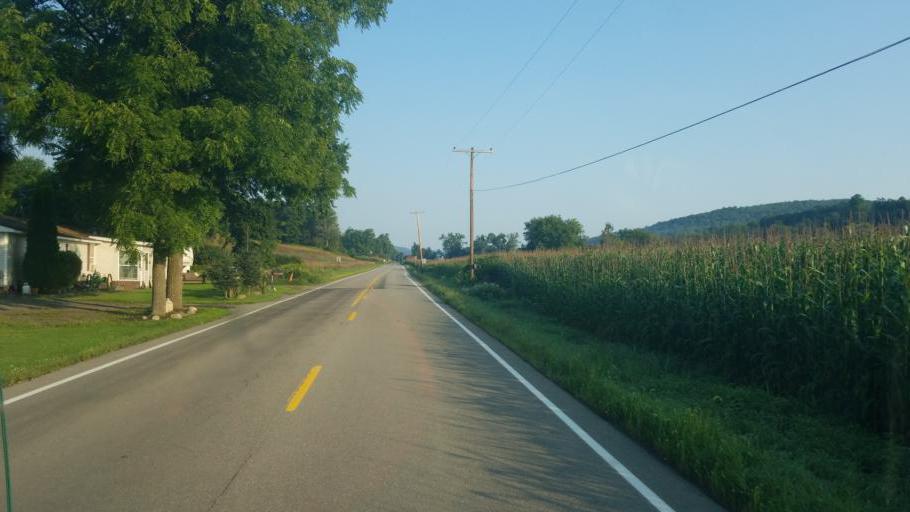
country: US
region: Pennsylvania
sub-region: Tioga County
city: Westfield
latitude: 41.9959
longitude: -77.4989
